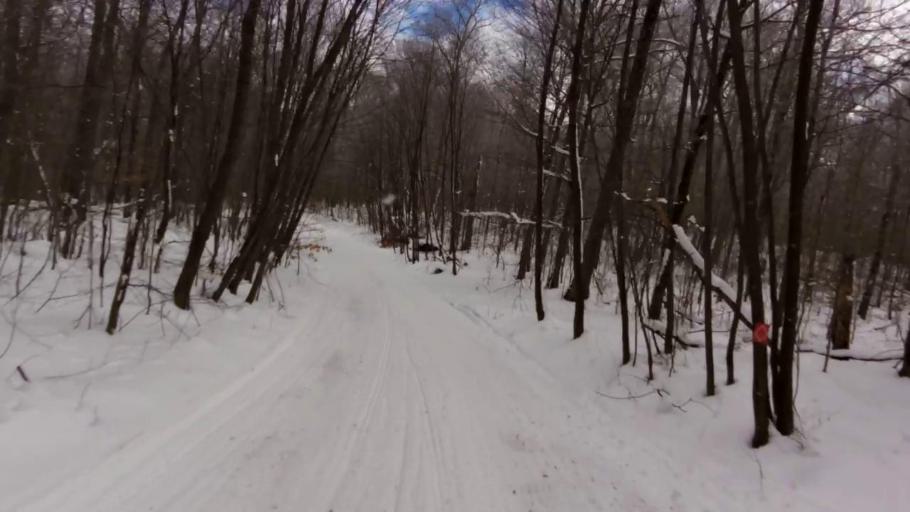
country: US
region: Pennsylvania
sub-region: McKean County
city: Bradford
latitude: 42.0042
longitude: -78.6714
